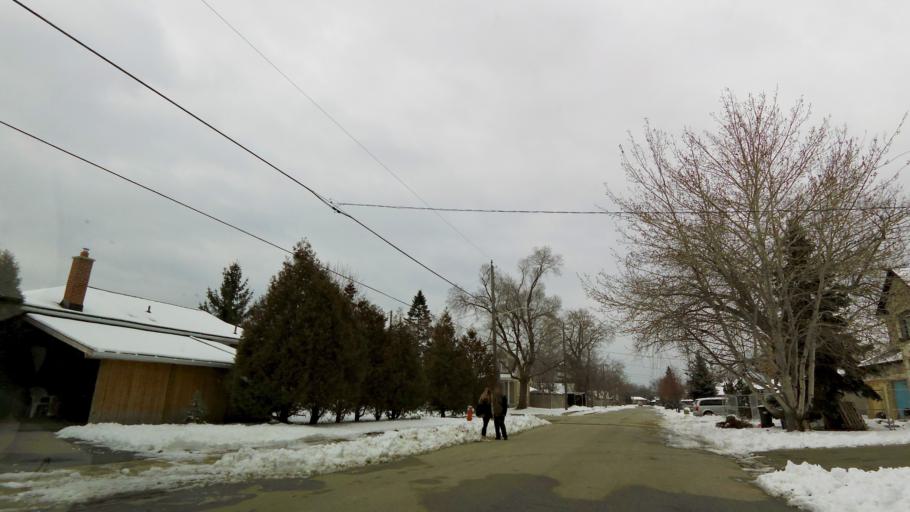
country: CA
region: Ontario
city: Etobicoke
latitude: 43.5805
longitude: -79.5663
